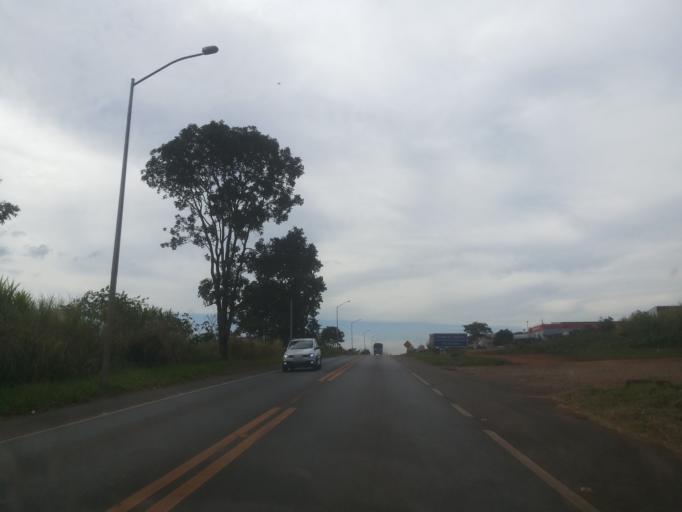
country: BR
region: Minas Gerais
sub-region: Ituiutaba
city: Ituiutaba
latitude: -18.9531
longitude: -49.4665
